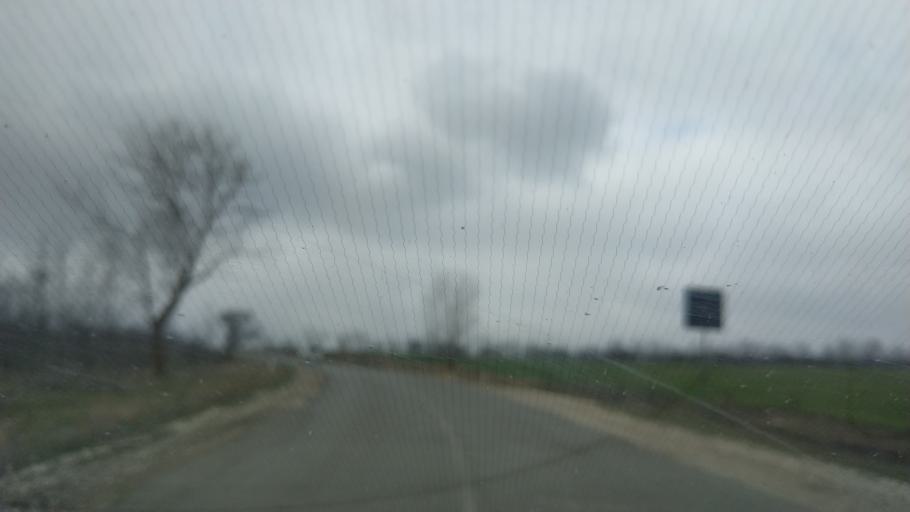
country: MD
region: Gagauzia
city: Bugeac
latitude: 46.3355
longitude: 28.7529
